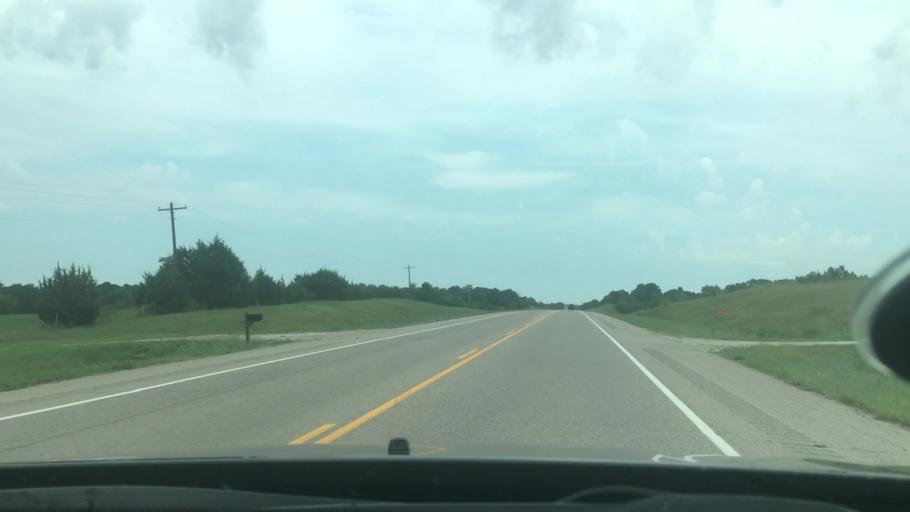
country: US
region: Oklahoma
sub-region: Seminole County
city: Konawa
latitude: 34.9938
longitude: -96.6791
